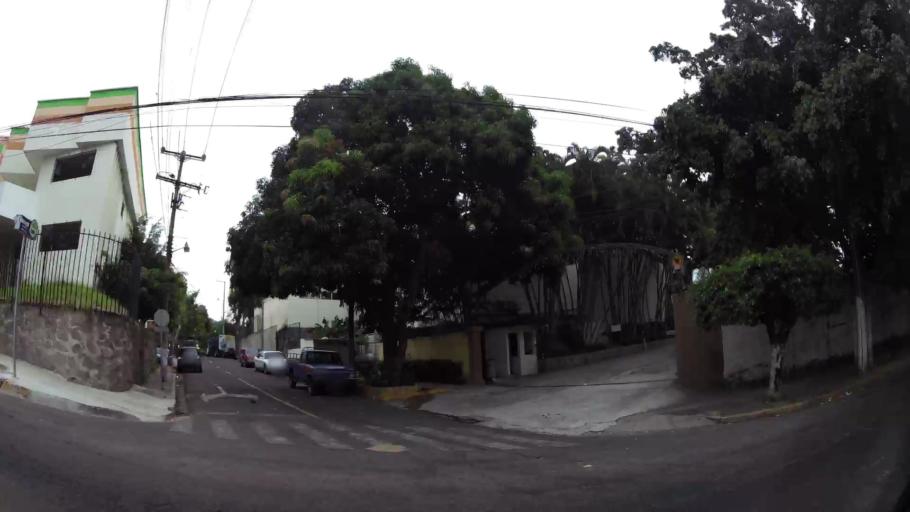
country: SV
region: San Salvador
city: Mejicanos
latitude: 13.7113
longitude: -89.2468
